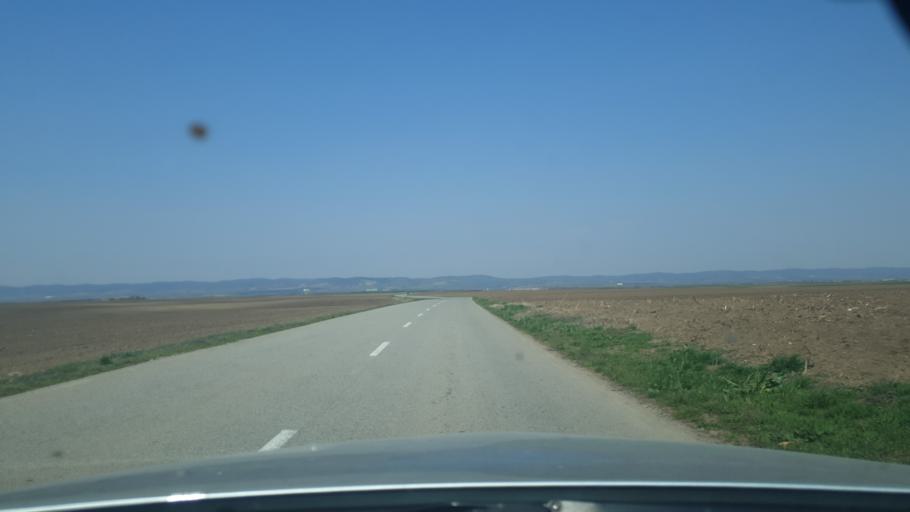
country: RS
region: Autonomna Pokrajina Vojvodina
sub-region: Sremski Okrug
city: Ruma
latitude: 45.0316
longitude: 19.7621
